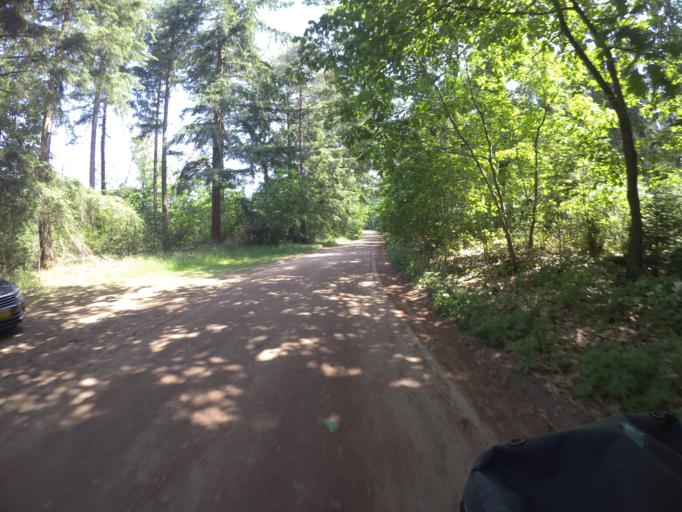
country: NL
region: Drenthe
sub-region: Gemeente De Wolden
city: Ruinen
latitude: 52.7304
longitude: 6.3836
